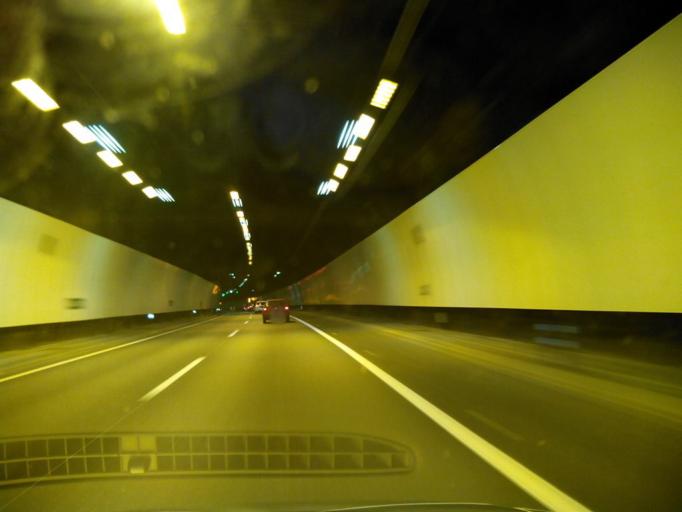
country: ES
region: Catalonia
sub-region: Provincia de Barcelona
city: La Roca del Valles
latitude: 41.5860
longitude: 2.3533
